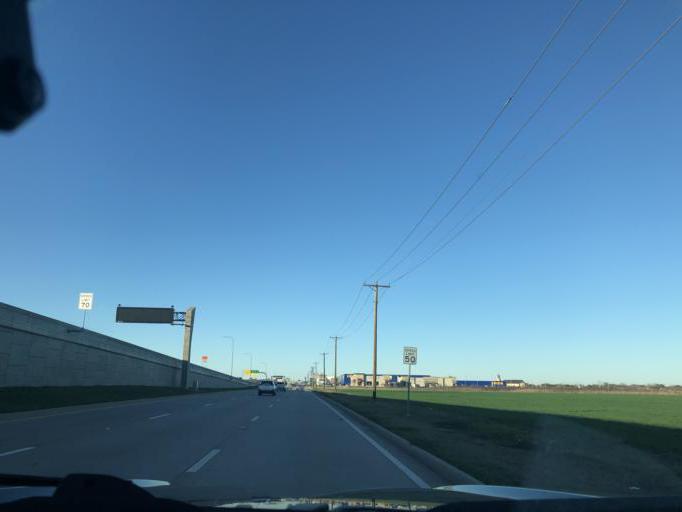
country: US
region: Texas
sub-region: Dallas County
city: Grand Prairie
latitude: 32.6837
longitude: -97.0235
